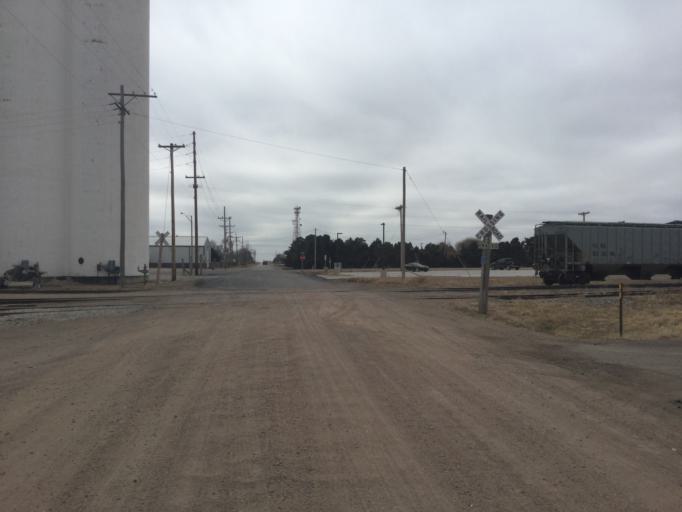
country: US
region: Kansas
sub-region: Haskell County
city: Sublette
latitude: 37.4816
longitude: -100.8529
